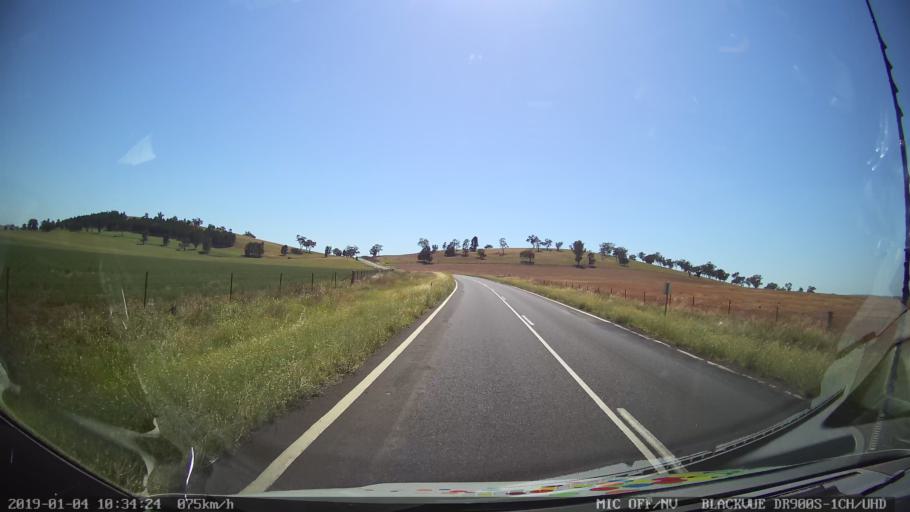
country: AU
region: New South Wales
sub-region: Cabonne
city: Canowindra
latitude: -33.3160
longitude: 148.6602
